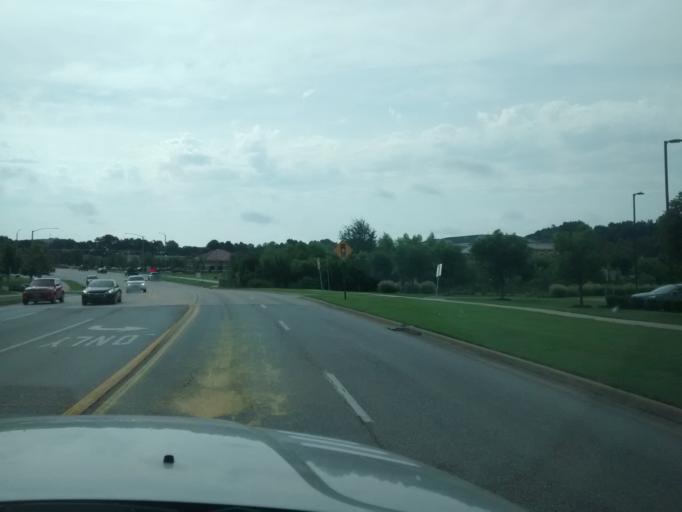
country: US
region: Arkansas
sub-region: Washington County
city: Johnson
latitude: 36.1208
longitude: -94.1402
